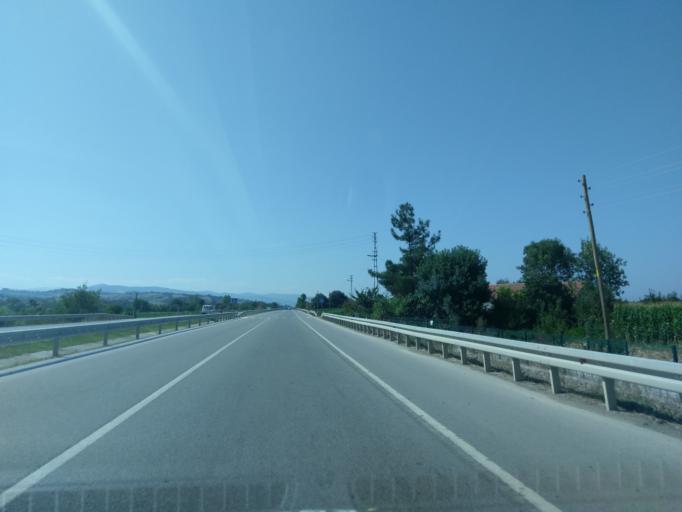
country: TR
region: Samsun
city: Alacam
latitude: 41.6087
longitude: 35.6643
